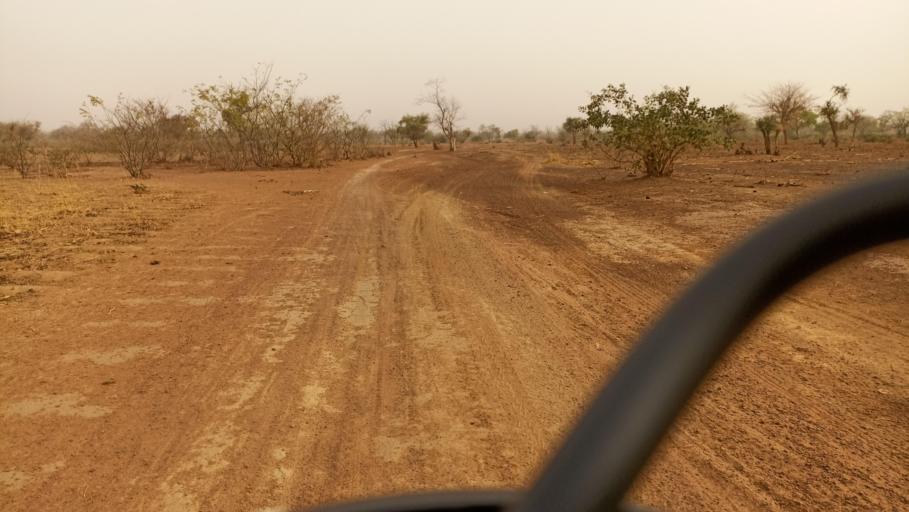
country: BF
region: Nord
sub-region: Province du Zondoma
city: Gourcy
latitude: 13.1553
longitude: -2.5947
